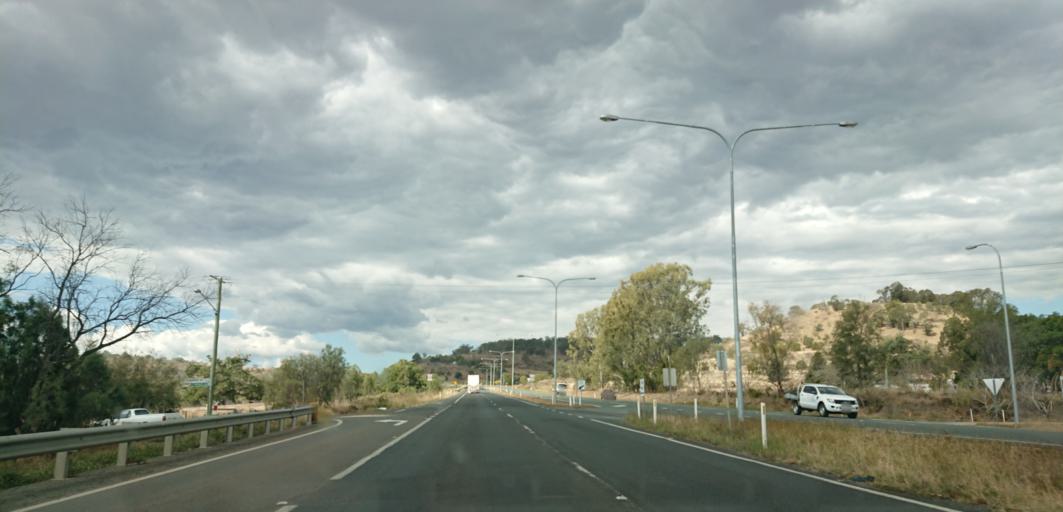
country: AU
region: Queensland
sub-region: Ipswich
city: Thagoona
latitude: -27.5507
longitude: 152.5074
